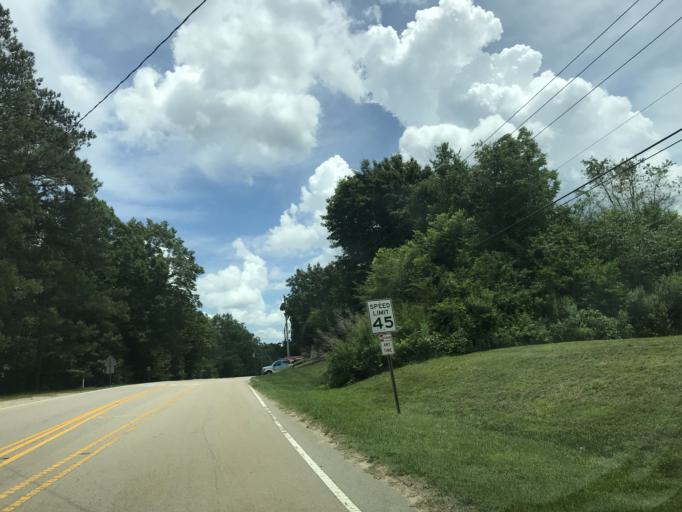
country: US
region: North Carolina
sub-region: Wake County
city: West Raleigh
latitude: 35.9089
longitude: -78.6608
